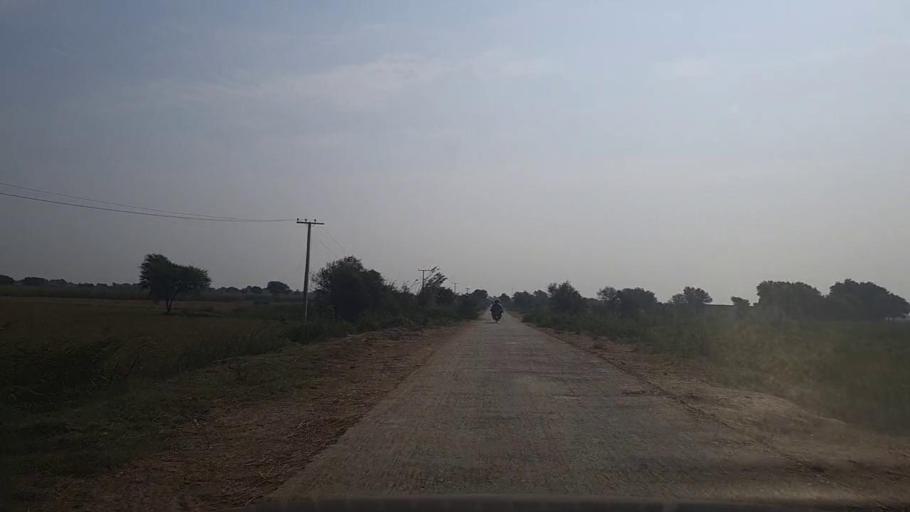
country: PK
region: Sindh
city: Bulri
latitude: 24.9742
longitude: 68.3240
